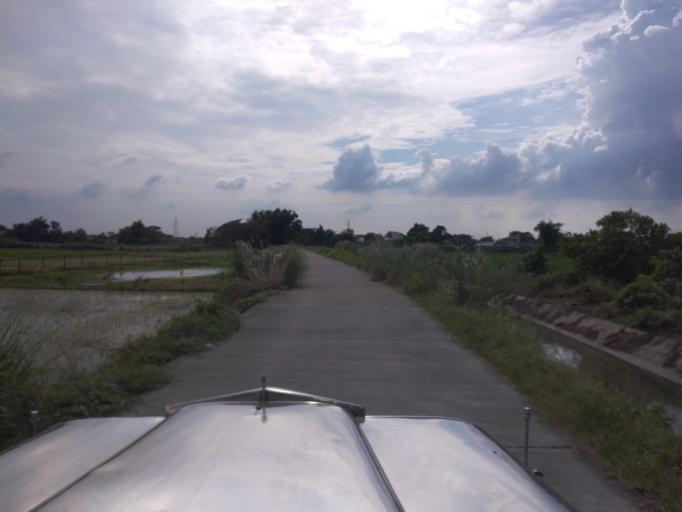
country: PH
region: Central Luzon
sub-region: Province of Pampanga
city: San Patricio
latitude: 15.1092
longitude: 120.7092
